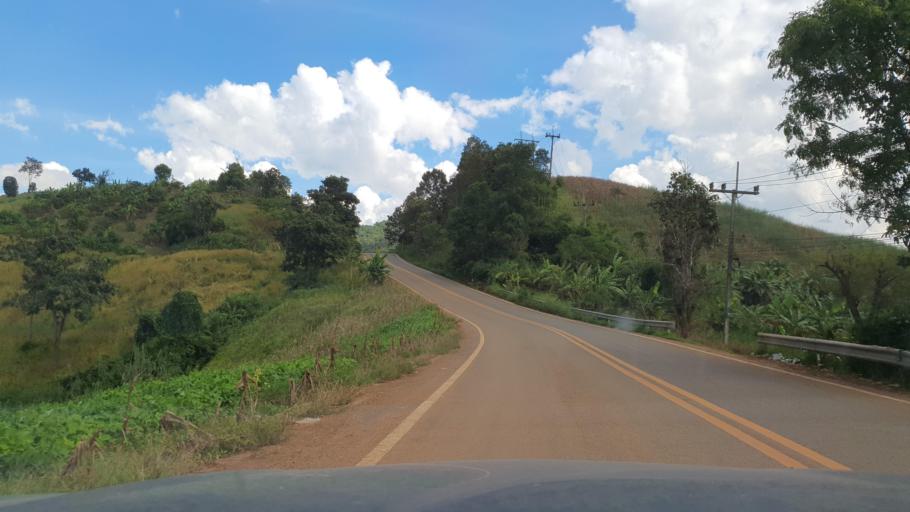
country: TH
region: Chiang Rai
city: Wiang Pa Pao
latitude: 19.3094
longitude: 99.4111
